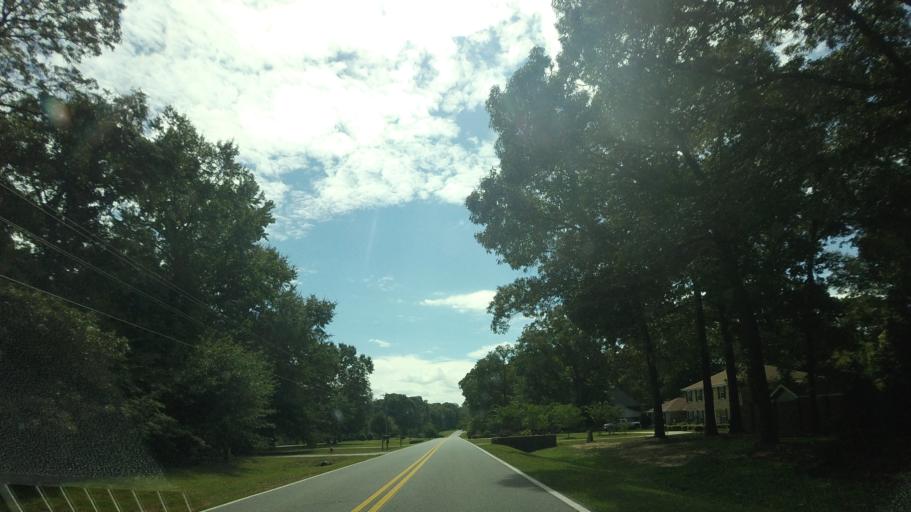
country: US
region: Georgia
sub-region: Houston County
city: Centerville
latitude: 32.5895
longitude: -83.7042
